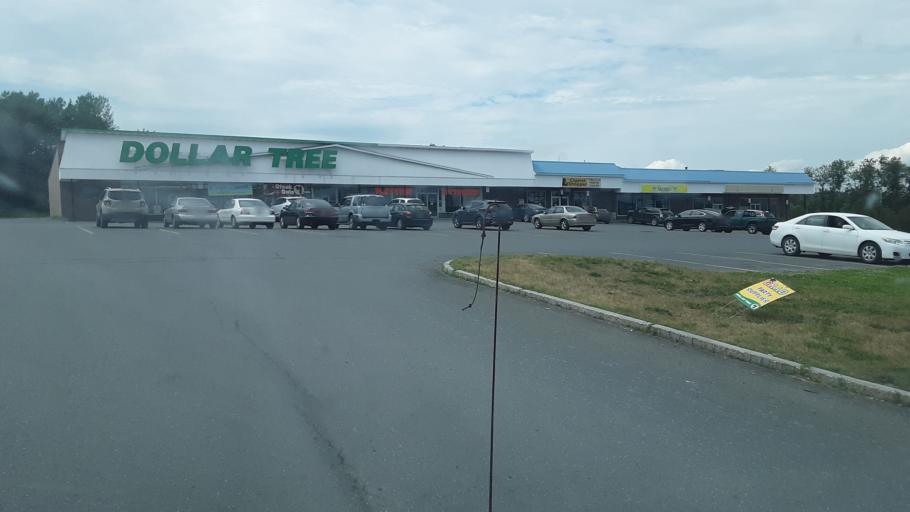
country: US
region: Maine
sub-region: Aroostook County
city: Caribou
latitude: 46.8694
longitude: -68.0039
